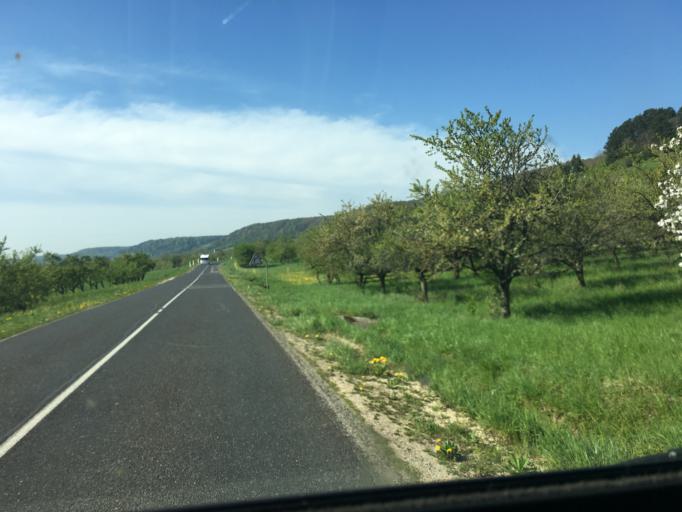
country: FR
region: Lorraine
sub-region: Departement de la Meuse
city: Vigneulles-les-Hattonchatel
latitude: 48.9194
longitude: 5.6800
